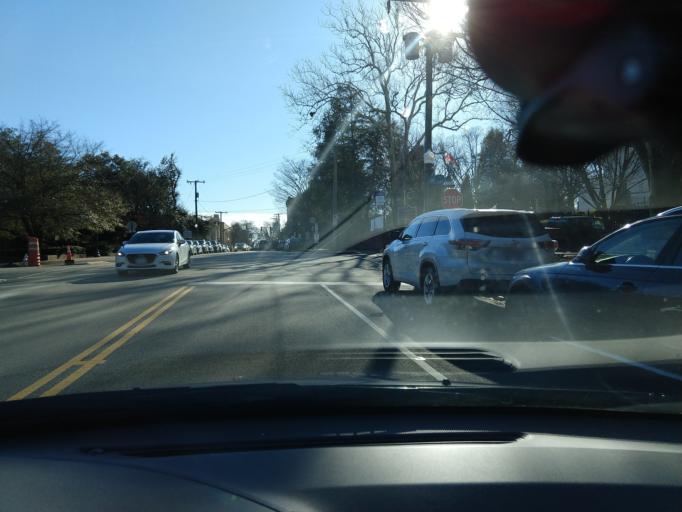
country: US
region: Virginia
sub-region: Henrico County
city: Montrose
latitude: 37.5323
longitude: -77.4200
